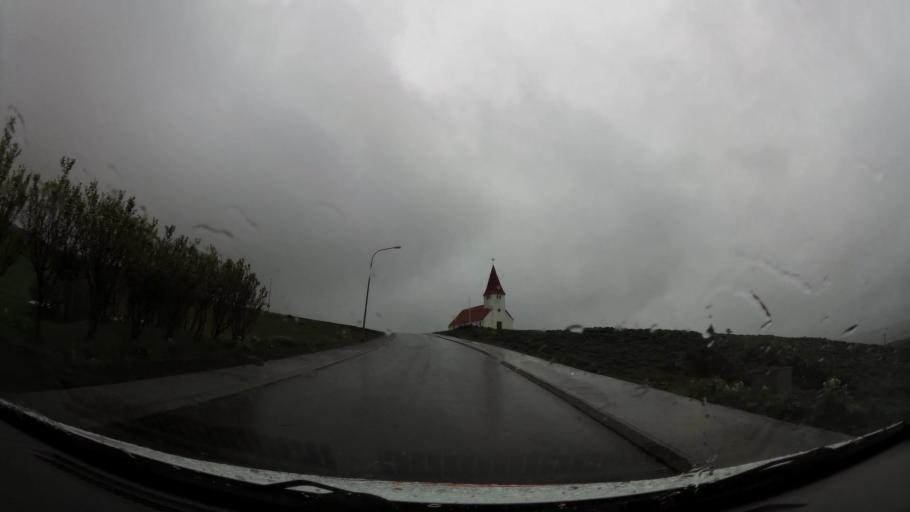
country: IS
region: South
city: Vestmannaeyjar
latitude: 63.4209
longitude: -19.0048
